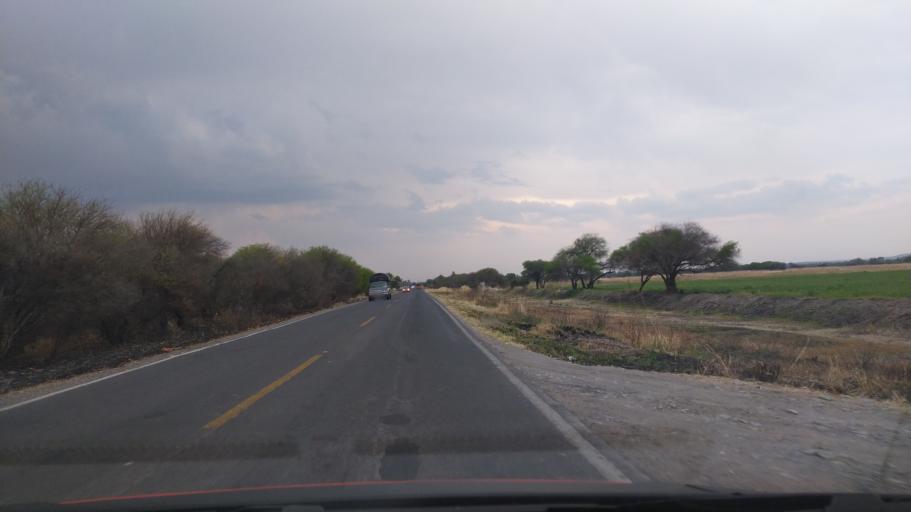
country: MX
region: Guanajuato
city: Ciudad Manuel Doblado
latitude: 20.7722
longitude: -101.9125
